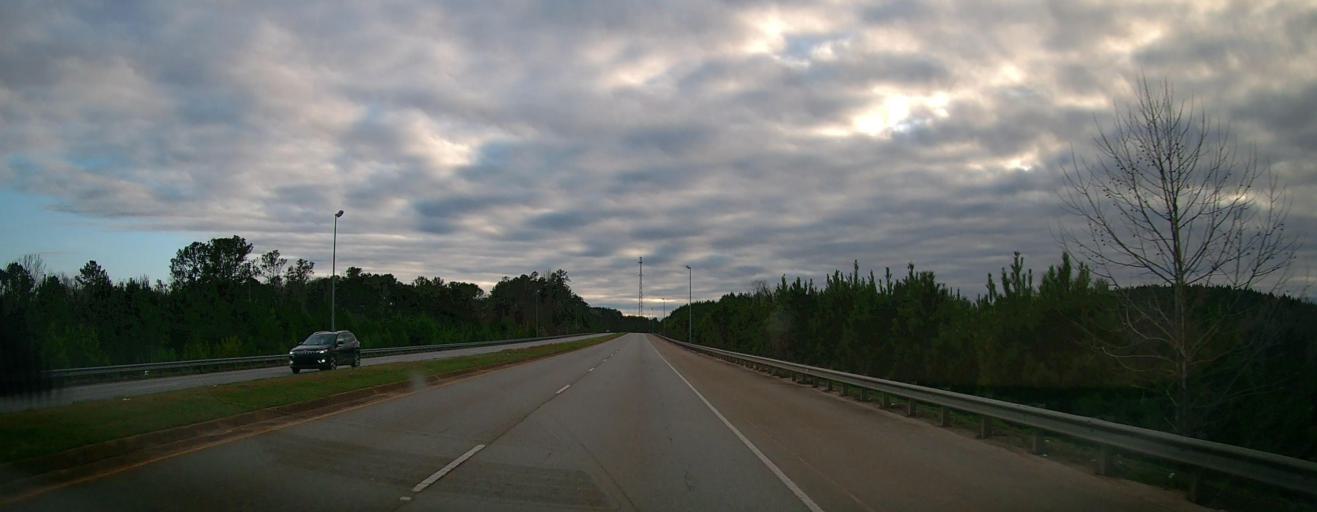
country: US
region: Georgia
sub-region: Troup County
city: West Point
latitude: 32.9050
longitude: -85.1268
